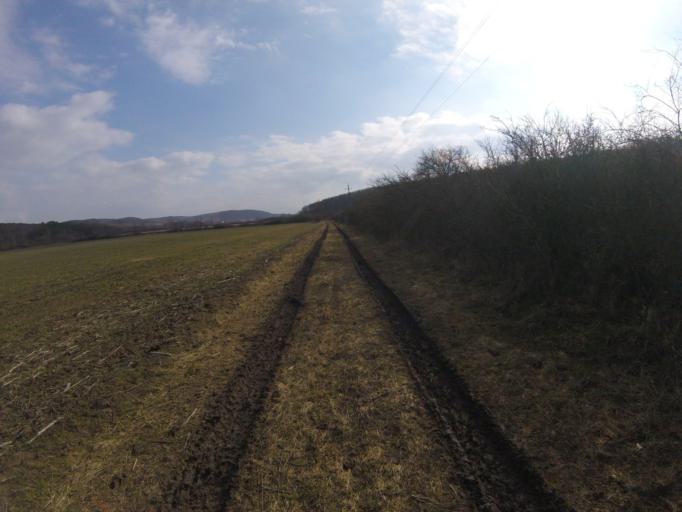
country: HU
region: Heves
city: Egerszalok
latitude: 47.8507
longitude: 20.3228
